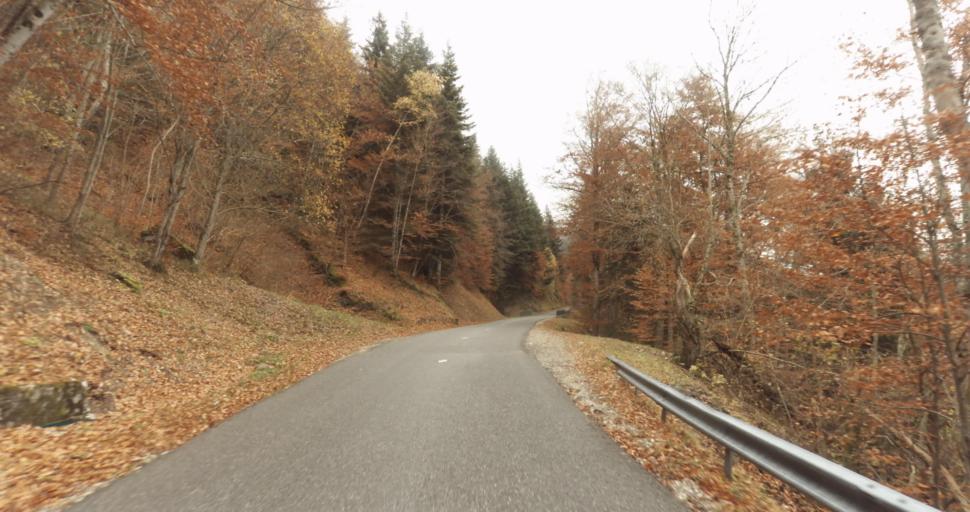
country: FR
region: Rhone-Alpes
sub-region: Departement de la Haute-Savoie
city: Thorens-Glieres
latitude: 45.9726
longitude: 6.2931
